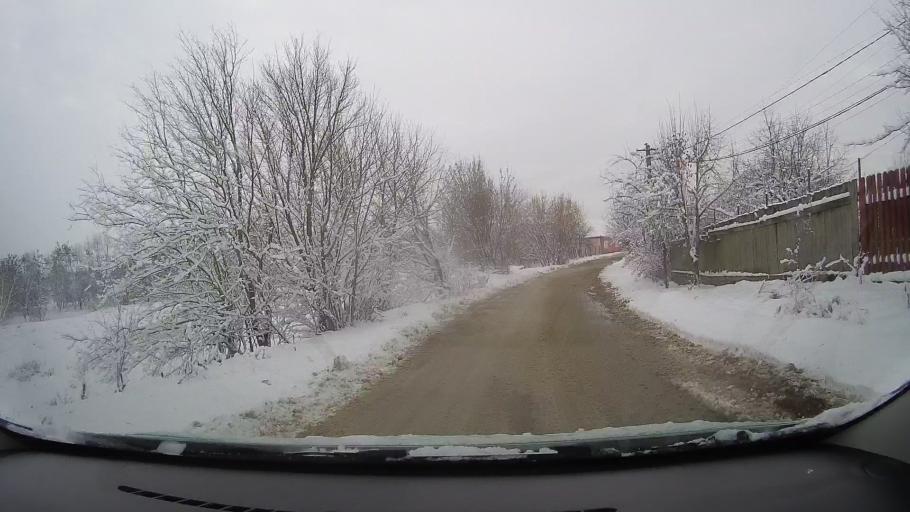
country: RO
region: Alba
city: Vurpar
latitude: 45.9806
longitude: 23.4816
